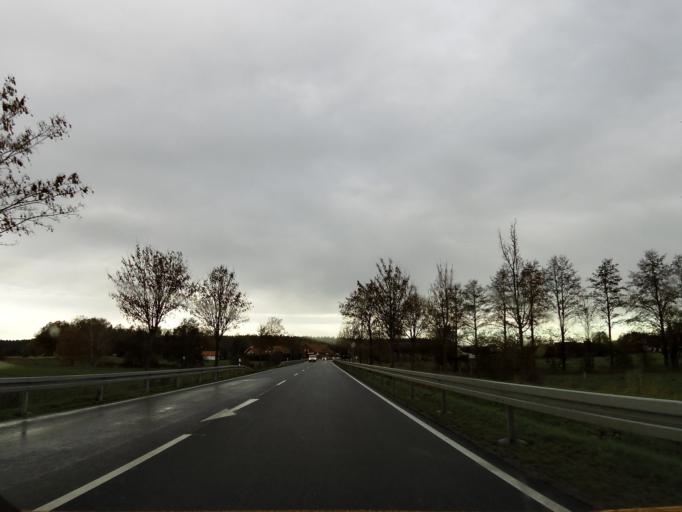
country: DE
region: Saxony-Anhalt
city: Gardelegen
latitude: 52.5504
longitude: 11.3636
